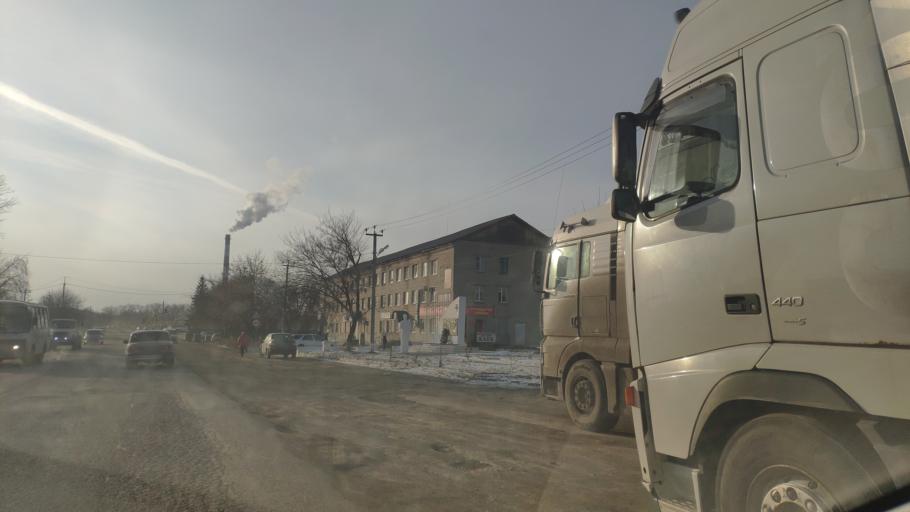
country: RU
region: Kurgan
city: Shadrinsk
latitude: 56.0864
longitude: 63.6710
